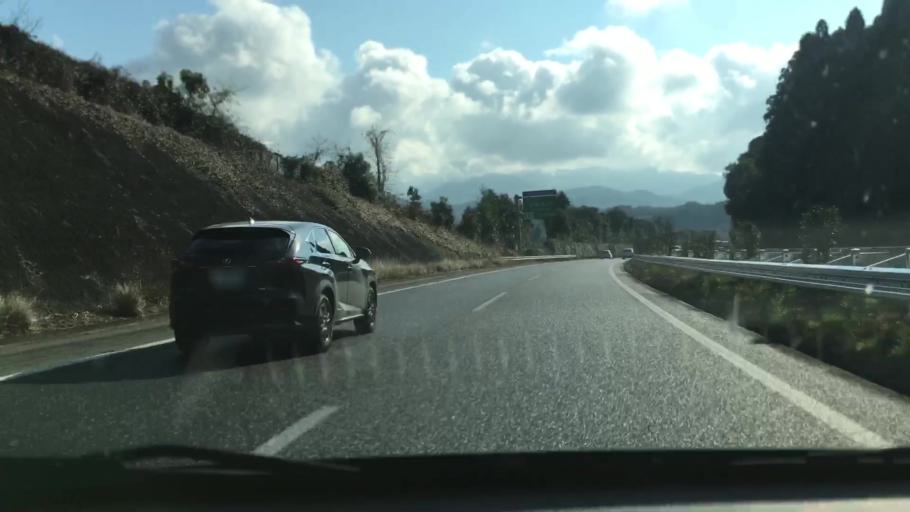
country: JP
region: Kumamoto
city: Matsubase
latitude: 32.5863
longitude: 130.7166
